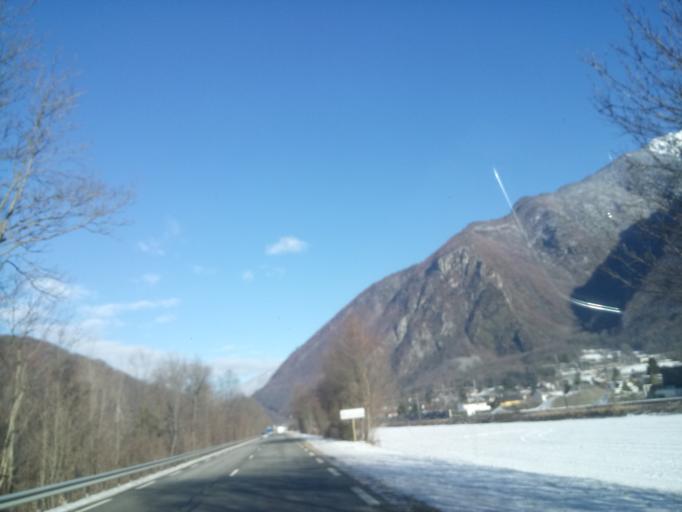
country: FR
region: Rhone-Alpes
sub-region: Departement de la Savoie
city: Saint-Remy-de-Maurienne
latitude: 45.4488
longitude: 6.2889
